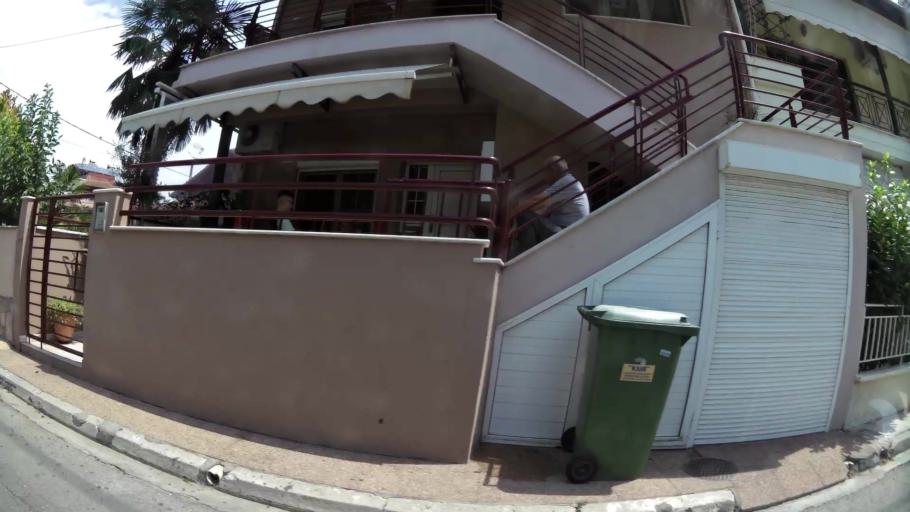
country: GR
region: Central Macedonia
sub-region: Nomos Pierias
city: Katerini
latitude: 40.2655
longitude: 22.5031
